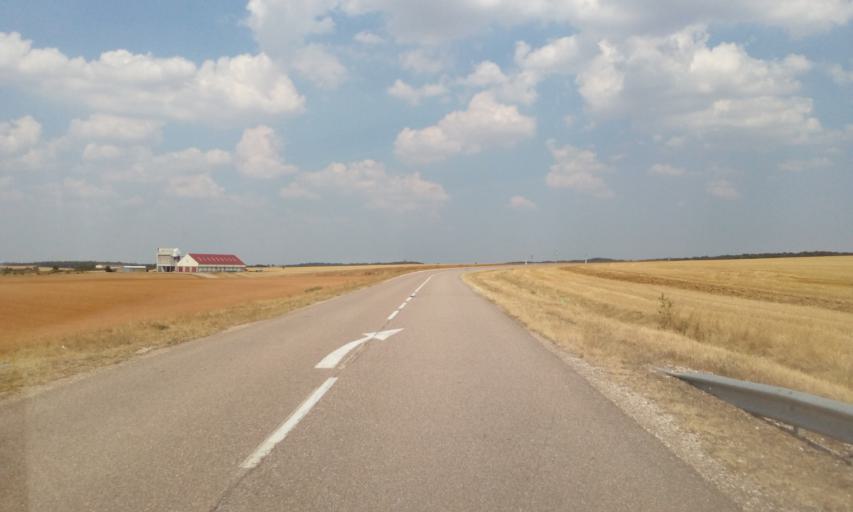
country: FR
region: Lorraine
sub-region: Departement de la Meuse
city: Vigneulles-les-Hattonchatel
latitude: 48.9661
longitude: 5.8606
